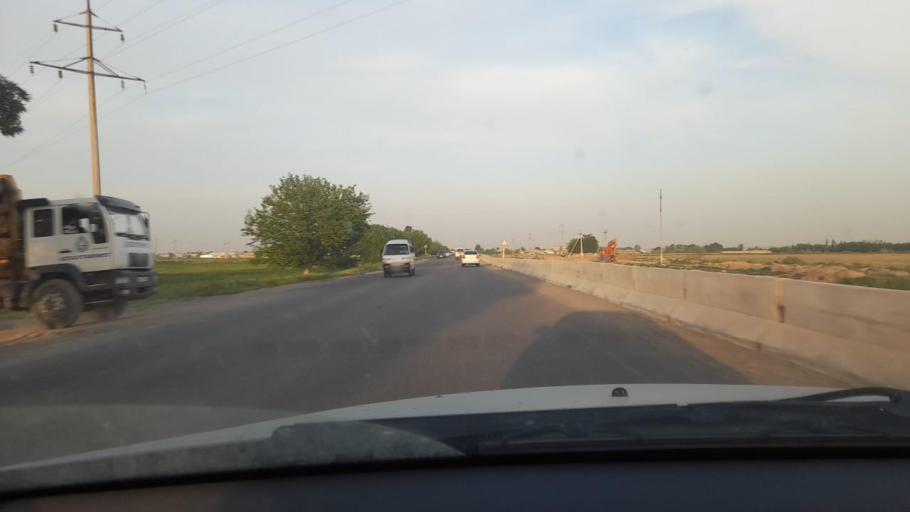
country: UZ
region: Sirdaryo
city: Guliston
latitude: 40.5080
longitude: 68.7352
